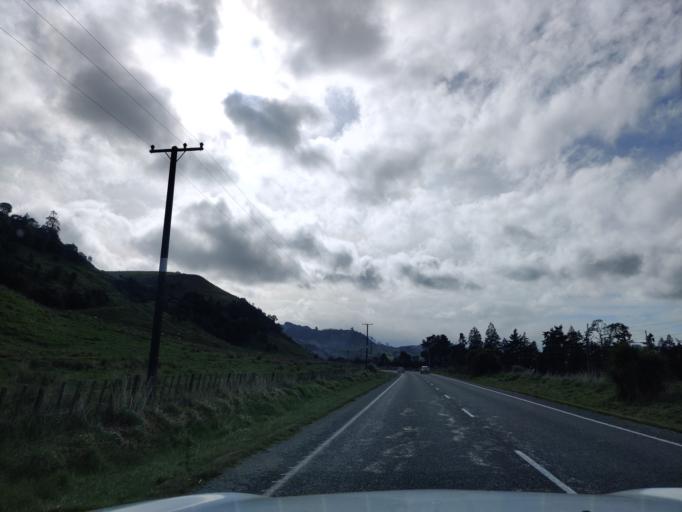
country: NZ
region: Manawatu-Wanganui
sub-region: Ruapehu District
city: Waiouru
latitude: -39.8486
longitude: 175.7360
